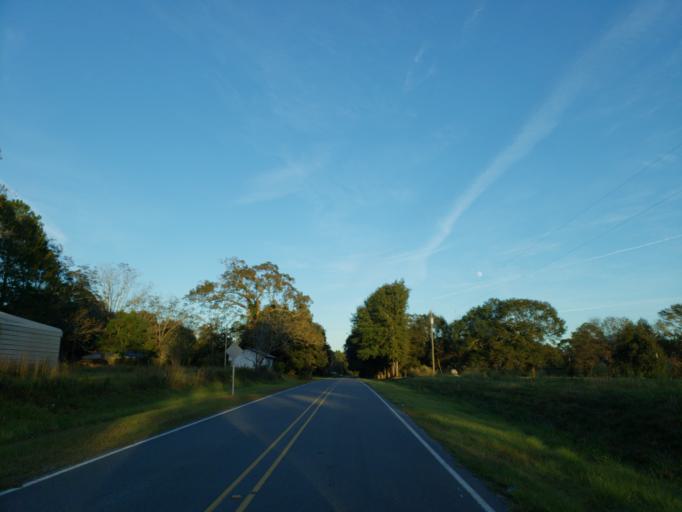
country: US
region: Mississippi
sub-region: Wayne County
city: Belmont
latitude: 31.4410
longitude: -88.5070
